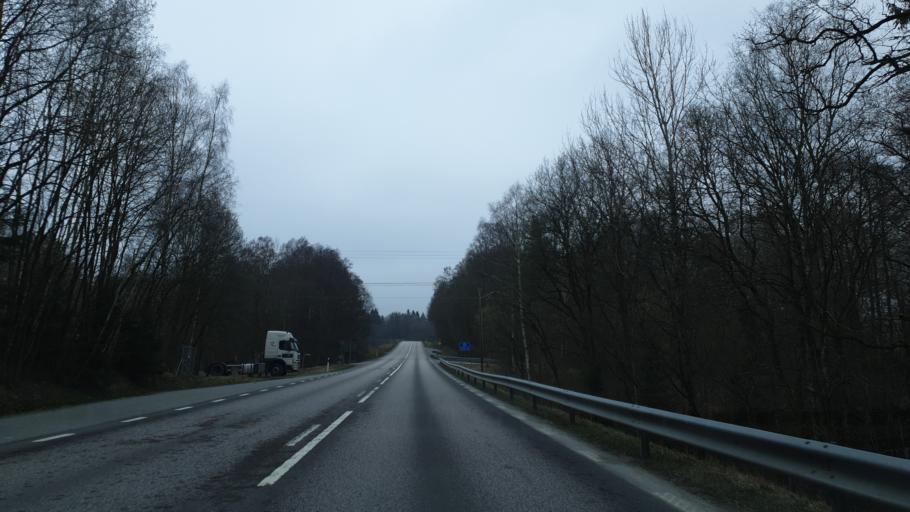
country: SE
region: Vaestra Goetaland
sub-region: Harryda Kommun
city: Ravlanda
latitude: 57.6125
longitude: 12.4353
